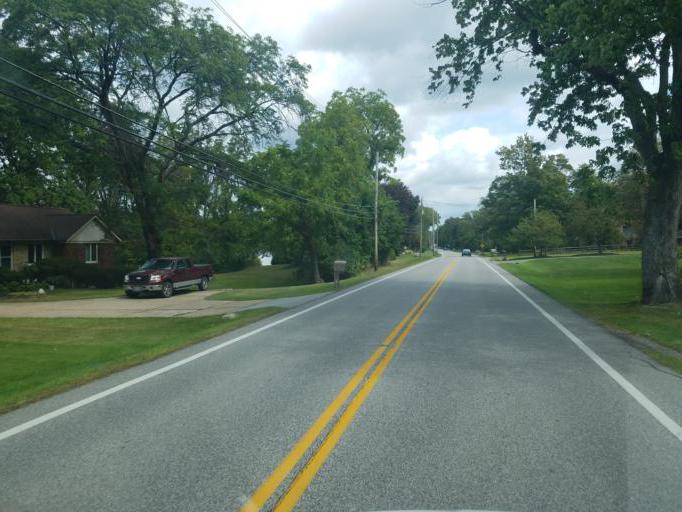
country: US
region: Ohio
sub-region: Lake County
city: Painesville
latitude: 41.7175
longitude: -81.2024
